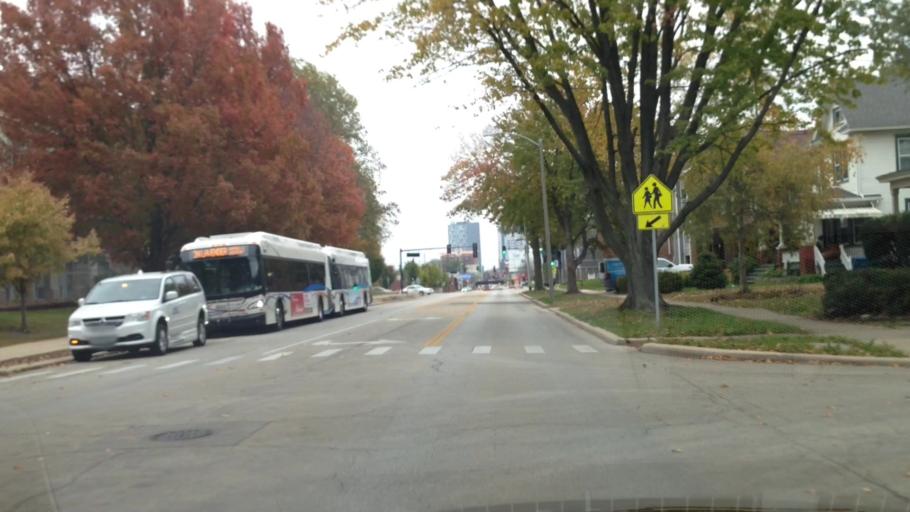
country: US
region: Illinois
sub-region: Champaign County
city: Champaign
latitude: 40.1101
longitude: -88.2485
